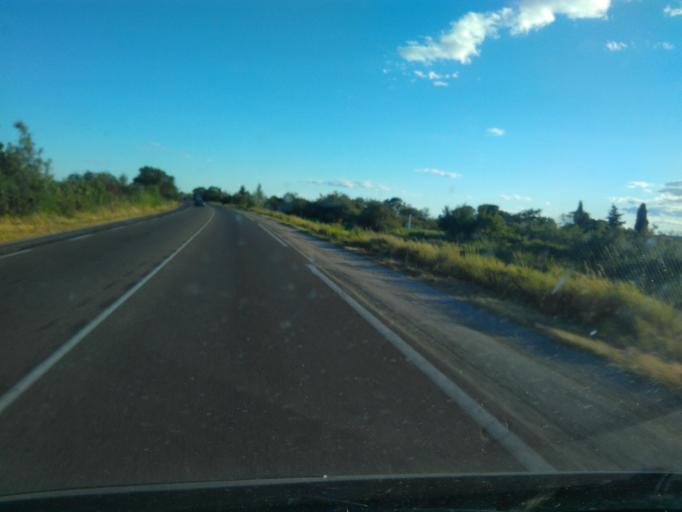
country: FR
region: Languedoc-Roussillon
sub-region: Departement de l'Herault
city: Saint-Just
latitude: 43.6168
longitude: 4.1136
